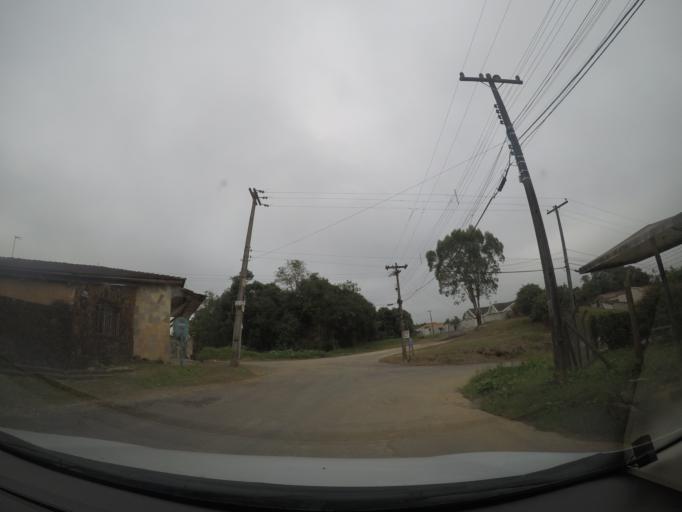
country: BR
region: Parana
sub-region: Colombo
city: Colombo
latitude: -25.3286
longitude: -49.2501
